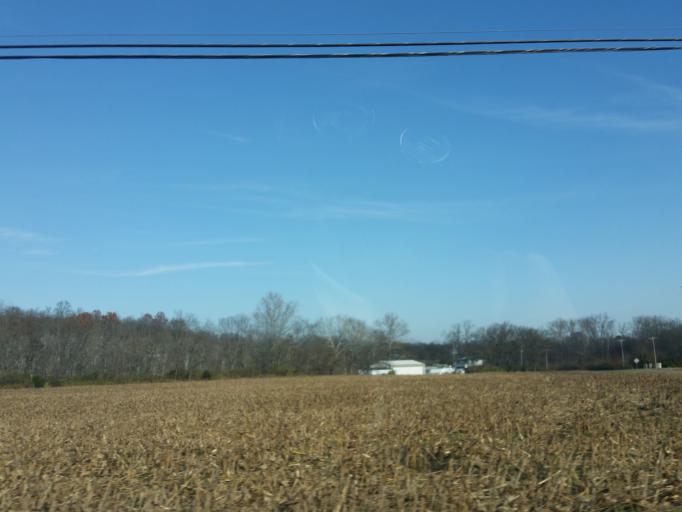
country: US
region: Ohio
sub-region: Butler County
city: Ross
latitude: 39.3603
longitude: -84.6480
